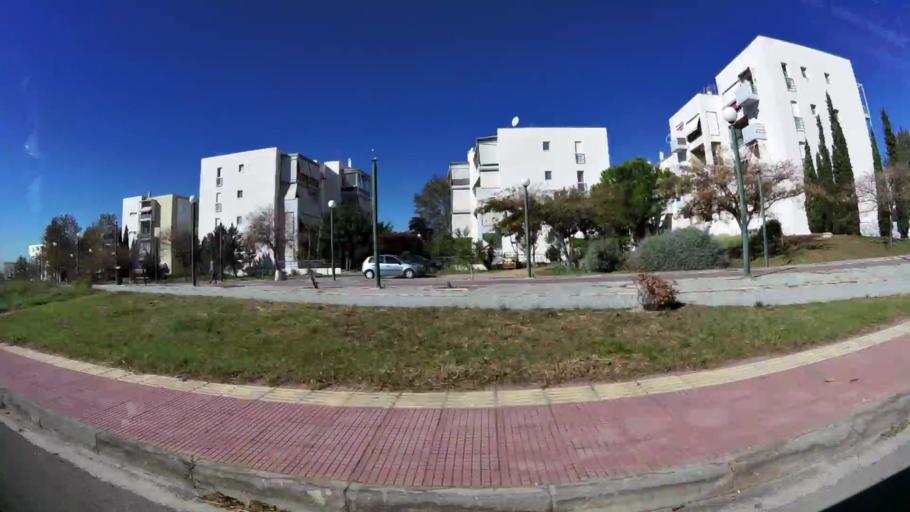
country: GR
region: Attica
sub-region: Nomarchia Anatolikis Attikis
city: Thrakomakedones
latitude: 38.1105
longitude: 23.7677
